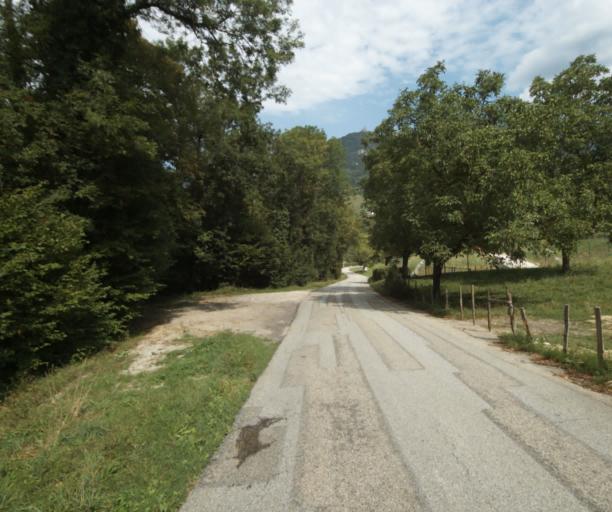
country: FR
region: Rhone-Alpes
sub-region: Departement de l'Isere
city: Saint-Egreve
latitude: 45.2454
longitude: 5.7234
